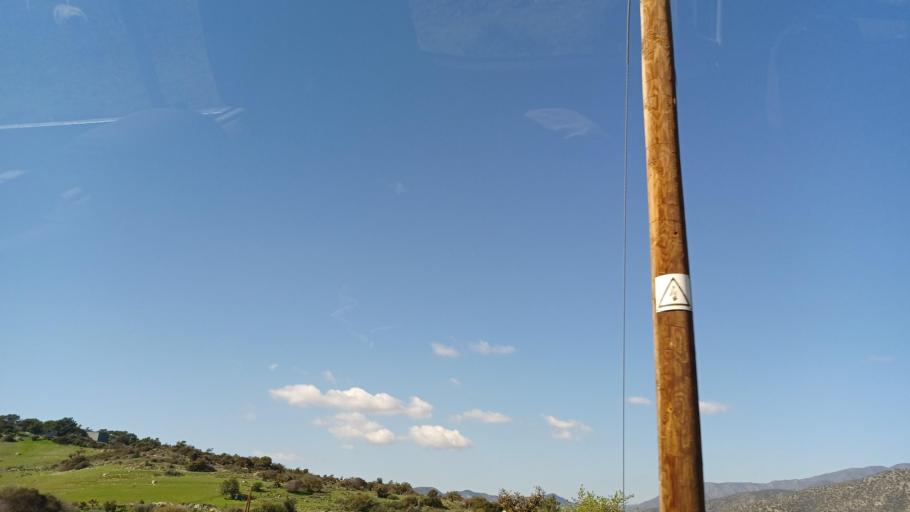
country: CY
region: Larnaka
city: Agios Tychon
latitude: 34.7496
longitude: 33.1317
